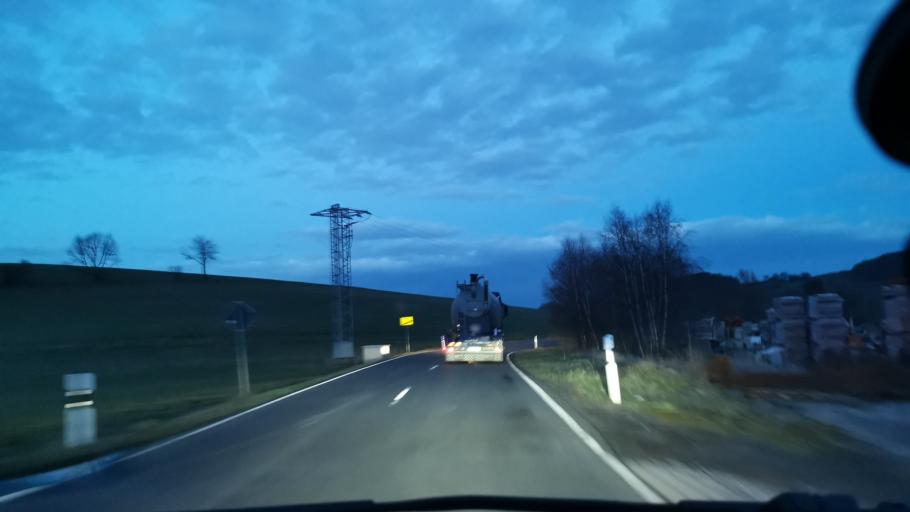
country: DE
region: Hesse
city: Waldkappel
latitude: 51.1141
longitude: 9.8244
